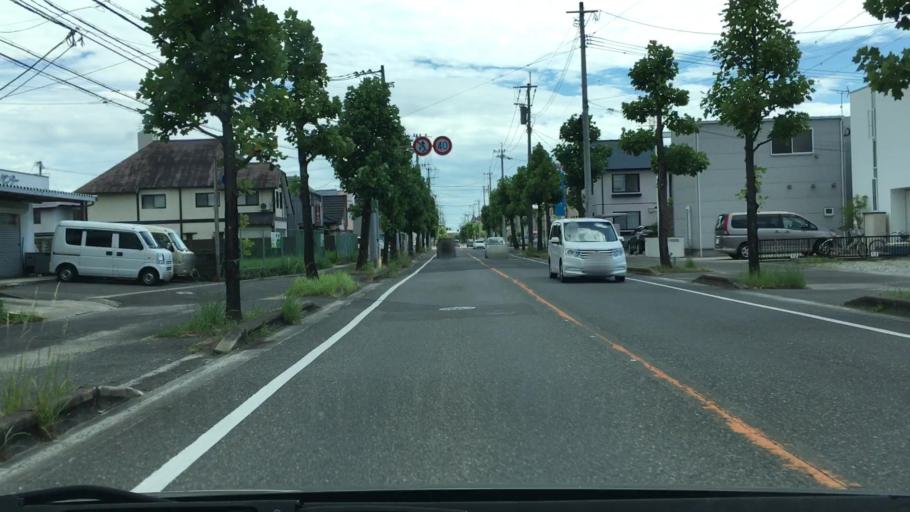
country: JP
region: Saga Prefecture
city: Saga-shi
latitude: 33.2718
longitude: 130.2866
